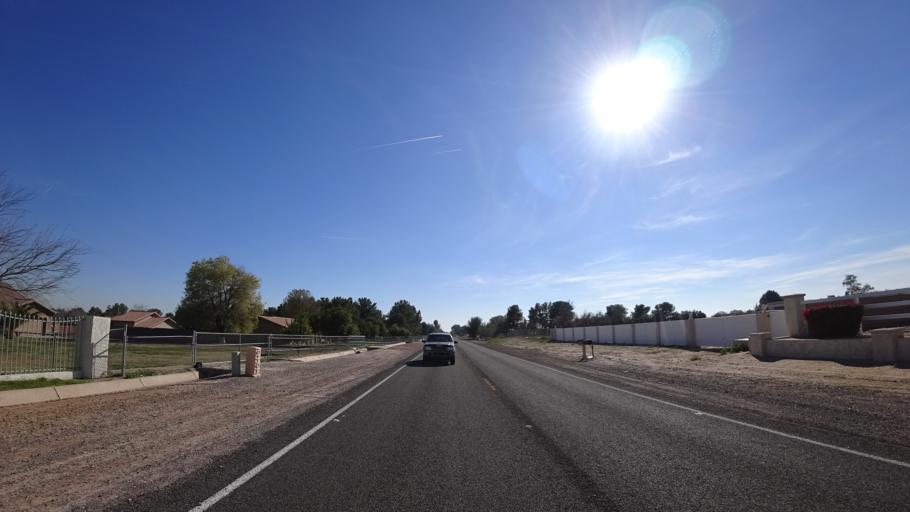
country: US
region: Arizona
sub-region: Maricopa County
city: Citrus Park
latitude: 33.5489
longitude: -112.4443
